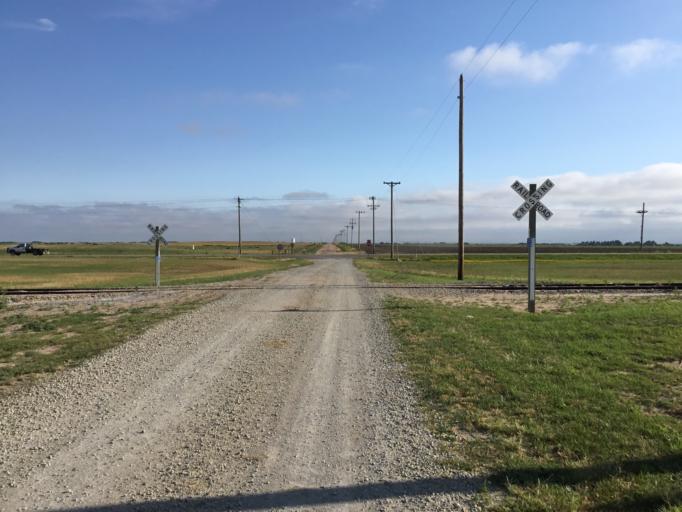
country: US
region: Kansas
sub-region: Barber County
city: Medicine Lodge
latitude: 37.4414
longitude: -98.4099
